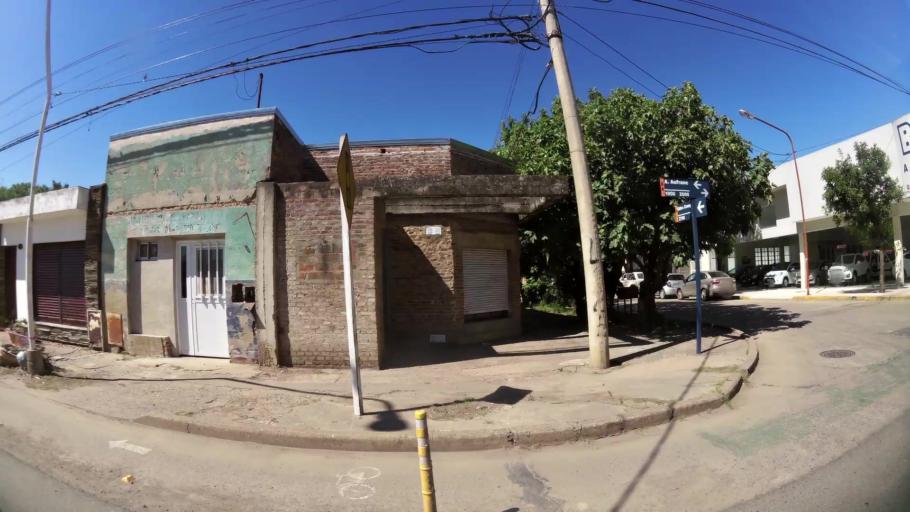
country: AR
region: Santa Fe
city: Esperanza
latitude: -31.4419
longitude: -60.9330
